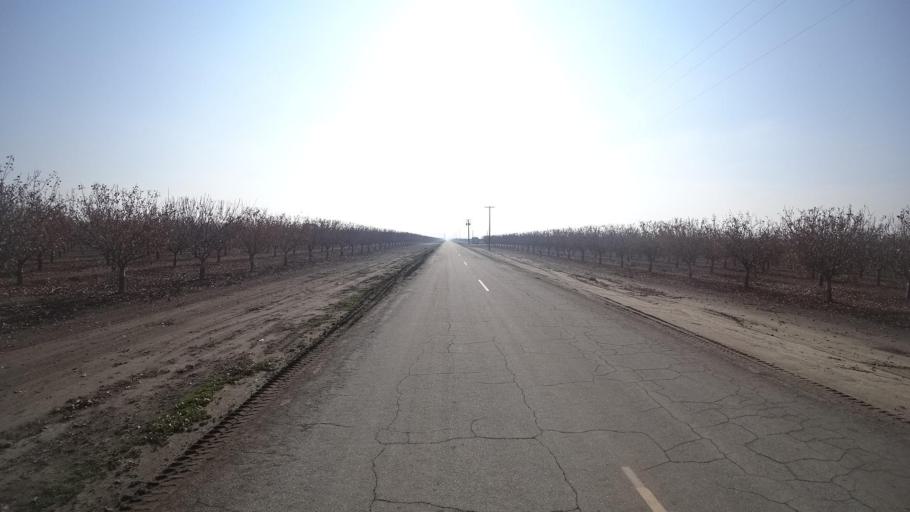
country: US
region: California
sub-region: Kern County
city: Buttonwillow
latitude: 35.3524
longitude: -119.3945
